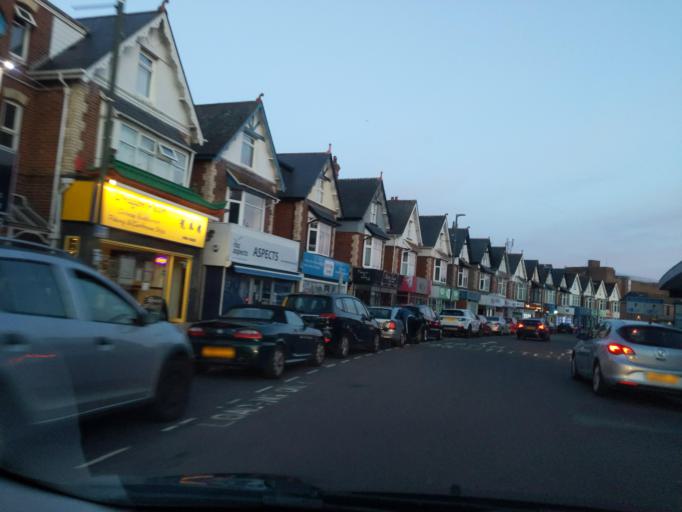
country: GB
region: England
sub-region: Borough of Torbay
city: Paignton
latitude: 50.4372
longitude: -3.5662
